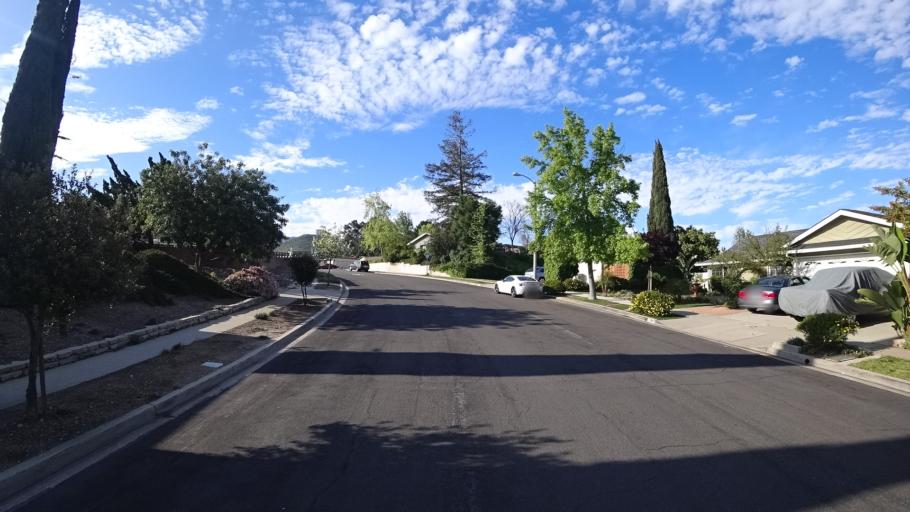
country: US
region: California
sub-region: Ventura County
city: Casa Conejo
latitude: 34.1743
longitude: -118.9532
